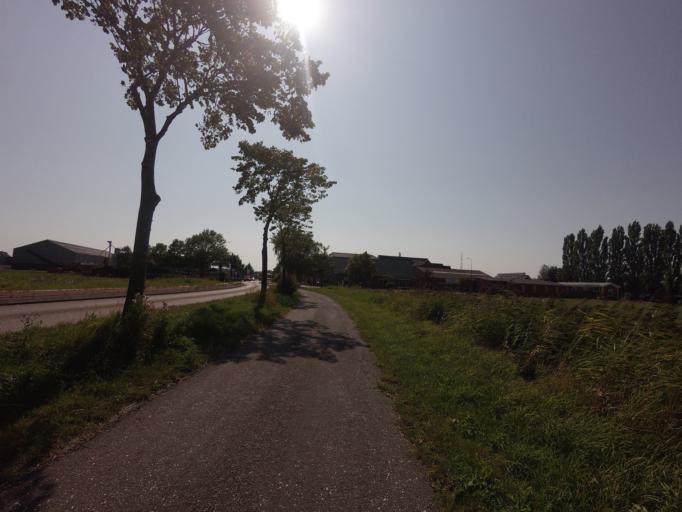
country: NL
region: Groningen
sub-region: Gemeente Zuidhorn
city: Grijpskerk
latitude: 53.2687
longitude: 6.3072
